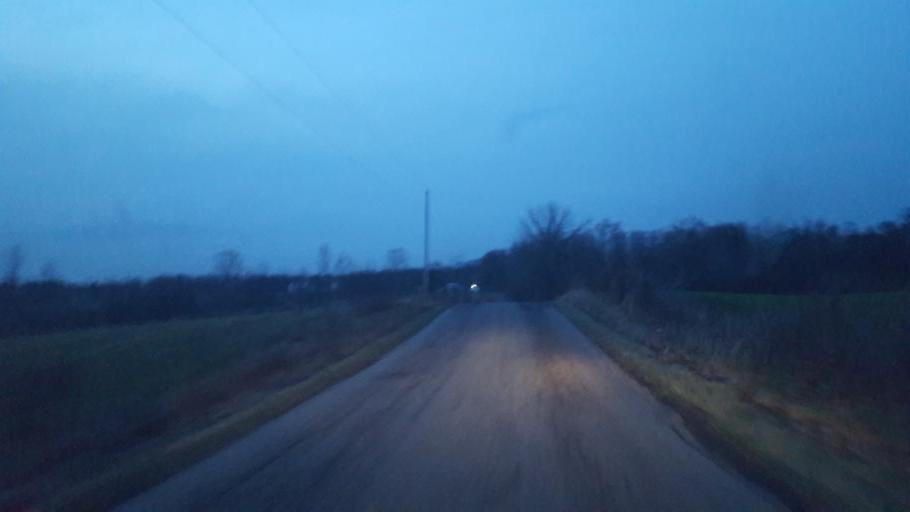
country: US
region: Ohio
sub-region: Knox County
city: Fredericktown
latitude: 40.5449
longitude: -82.5950
